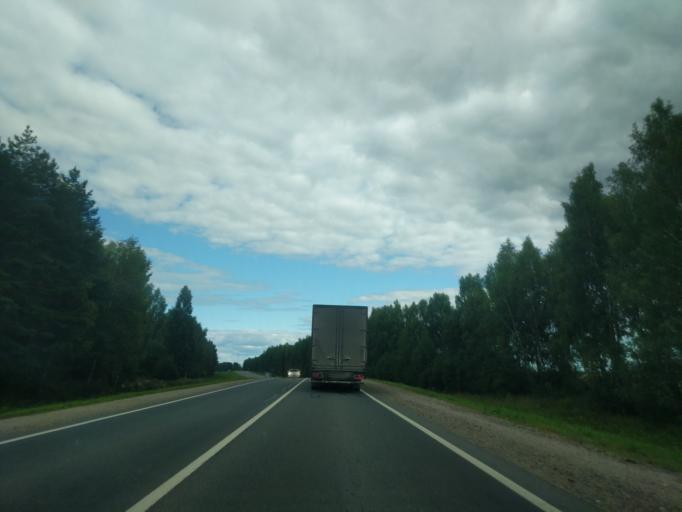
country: RU
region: Kostroma
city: Ostrovskoye
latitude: 57.8164
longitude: 42.2111
